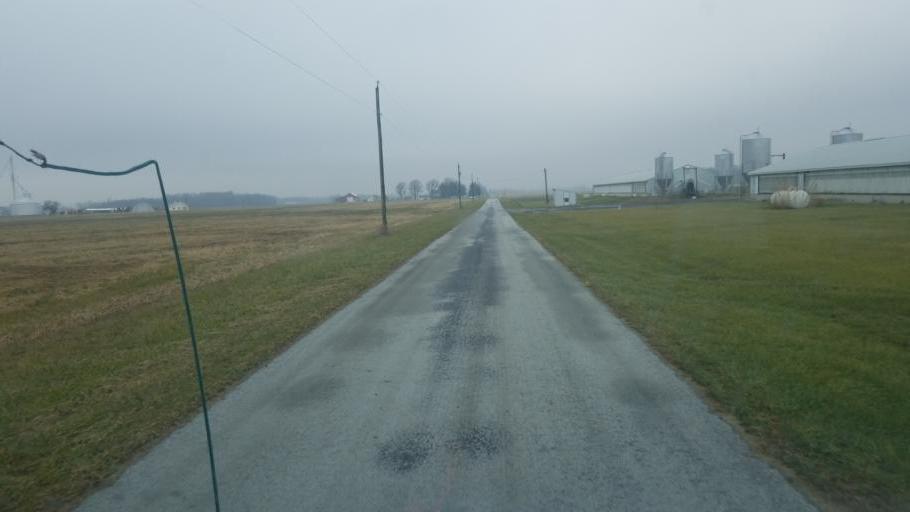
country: US
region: Ohio
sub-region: Hardin County
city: Forest
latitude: 40.6899
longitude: -83.4778
